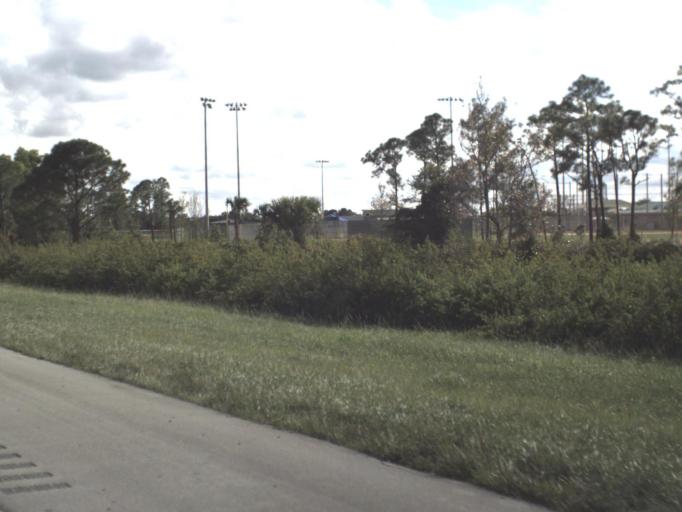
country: US
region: Florida
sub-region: Martin County
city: Palm City
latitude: 27.1788
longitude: -80.3165
